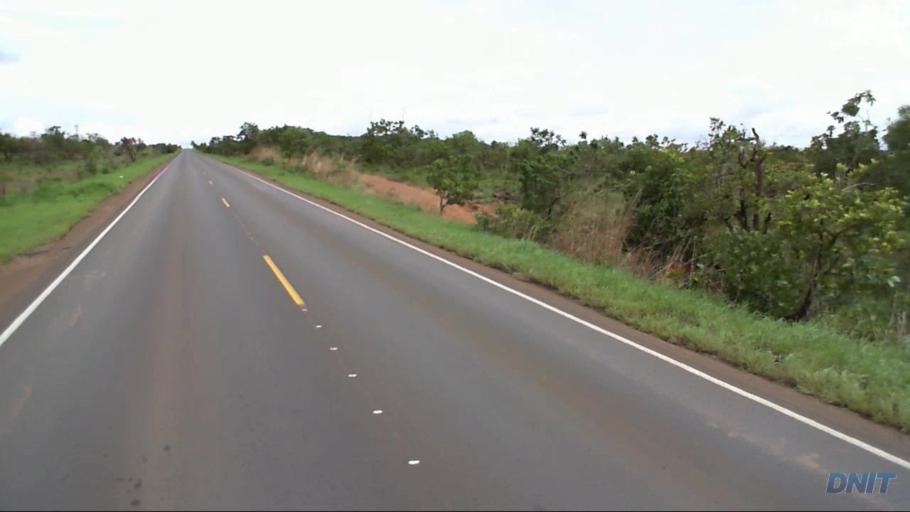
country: BR
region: Goias
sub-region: Padre Bernardo
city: Padre Bernardo
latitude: -15.2329
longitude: -48.2754
